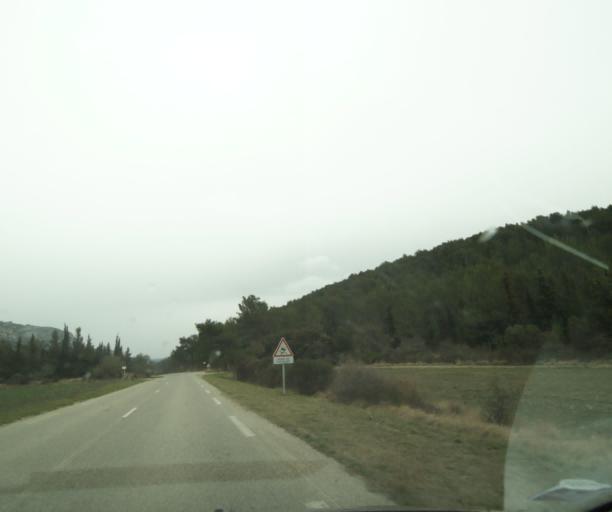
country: FR
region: Provence-Alpes-Cote d'Azur
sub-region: Departement des Bouches-du-Rhone
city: Saint-Marc-Jaumegarde
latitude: 43.5564
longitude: 5.5545
